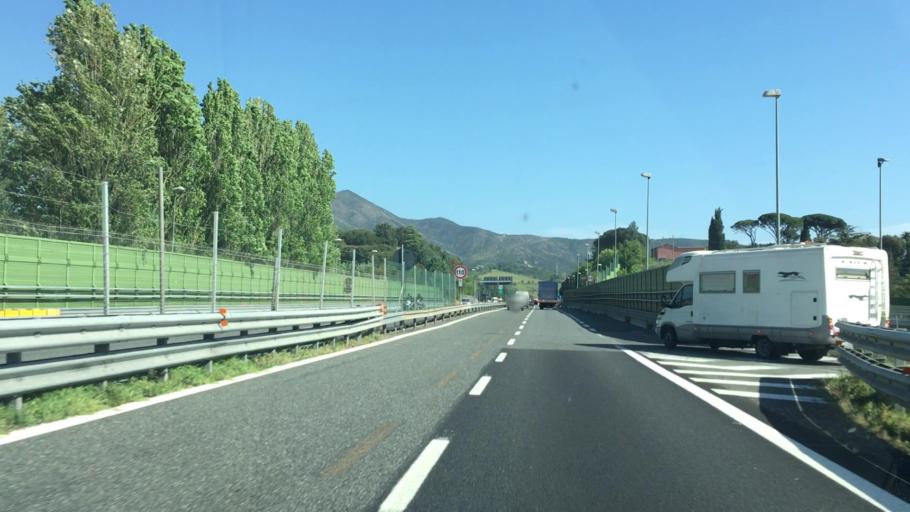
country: IT
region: Liguria
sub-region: Provincia di Genova
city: Sestri Levante
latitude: 44.2750
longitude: 9.4206
